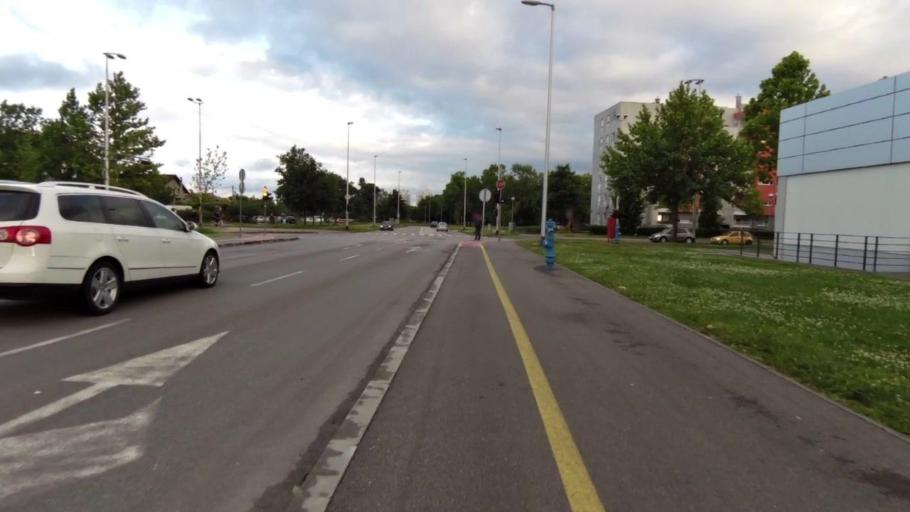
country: HR
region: Grad Zagreb
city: Dubrava
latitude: 45.8407
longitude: 16.0519
